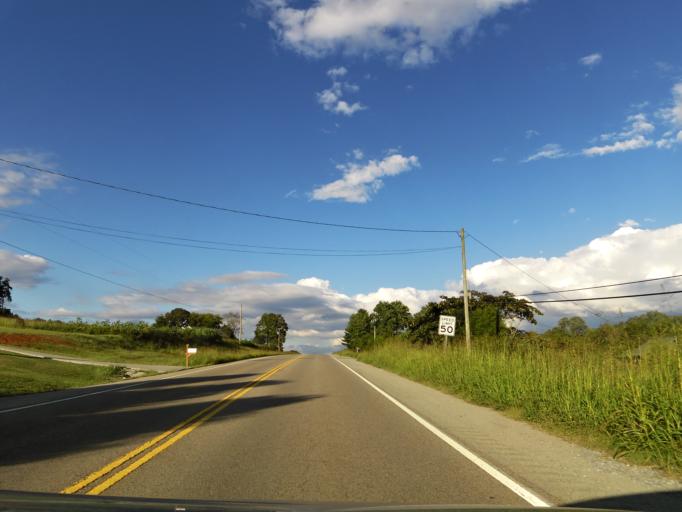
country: US
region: Tennessee
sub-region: Grainger County
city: Rutledge
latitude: 36.2398
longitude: -83.6113
